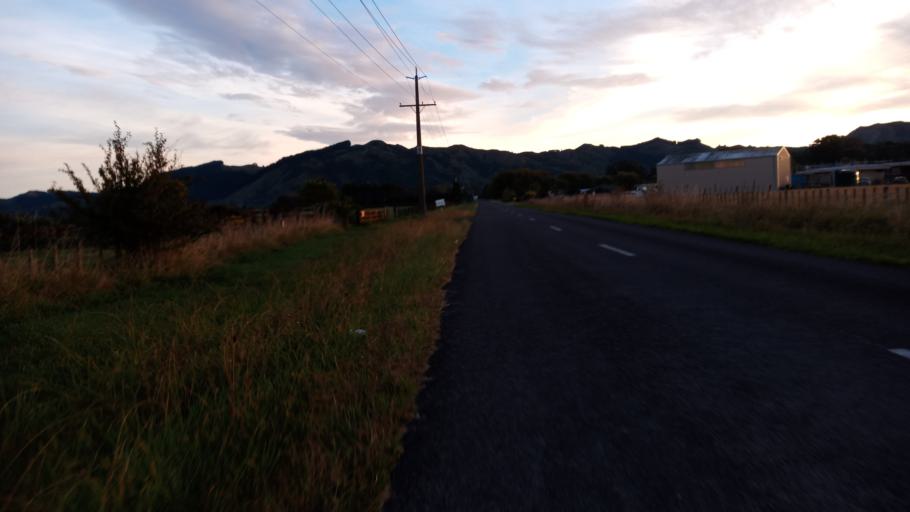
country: NZ
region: Gisborne
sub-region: Gisborne District
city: Gisborne
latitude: -38.6268
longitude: 177.9771
